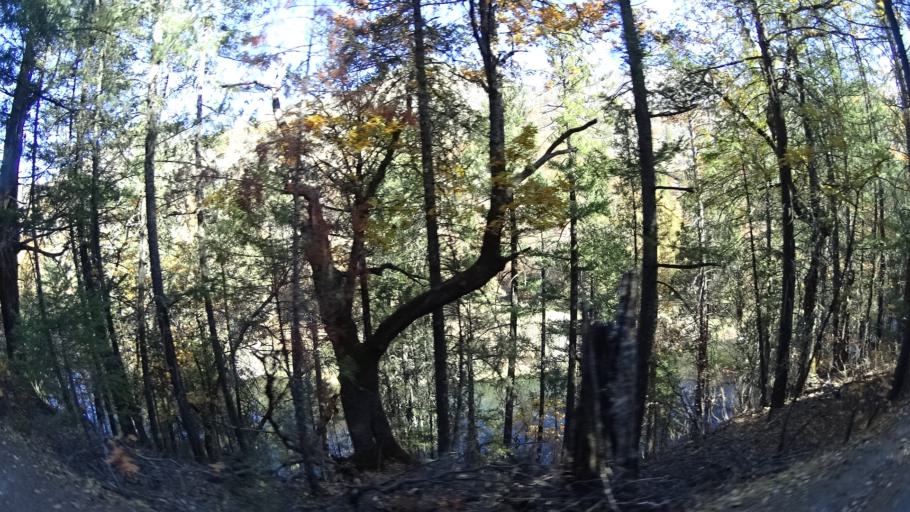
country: US
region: California
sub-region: Siskiyou County
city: Yreka
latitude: 41.8662
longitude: -122.8059
